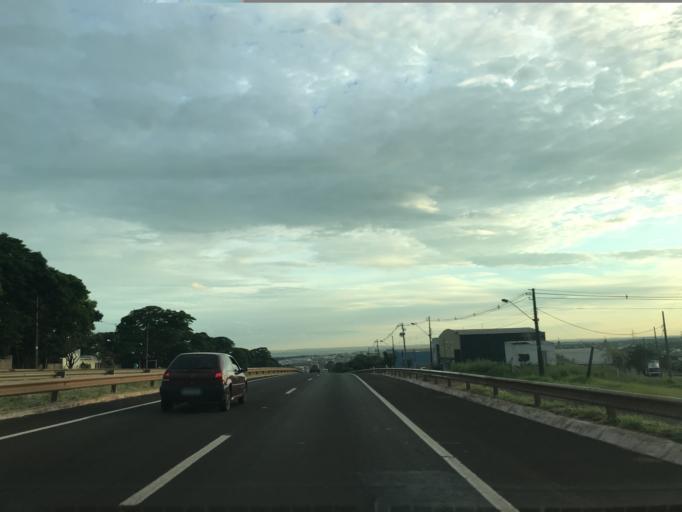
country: BR
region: Parana
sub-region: Maringa
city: Maringa
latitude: -23.4025
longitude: -51.9806
